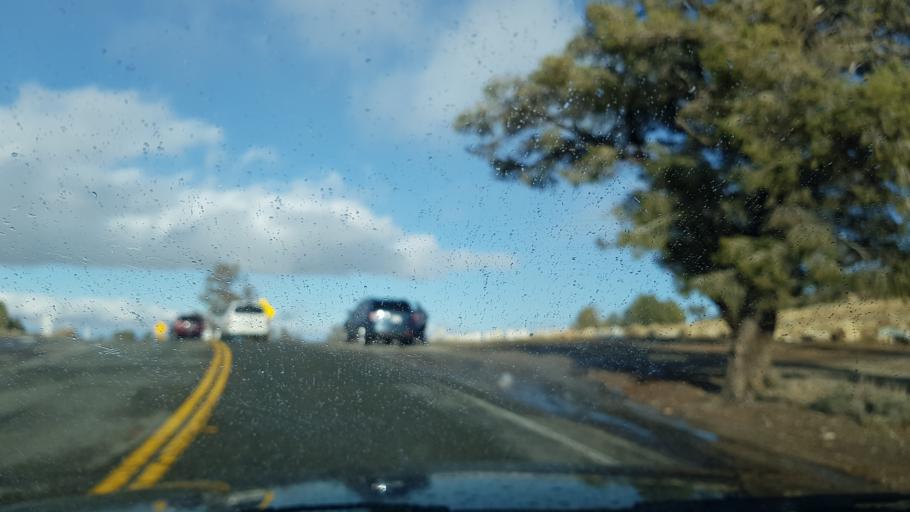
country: US
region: California
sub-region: San Bernardino County
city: Big Bear City
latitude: 34.2905
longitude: -116.8030
